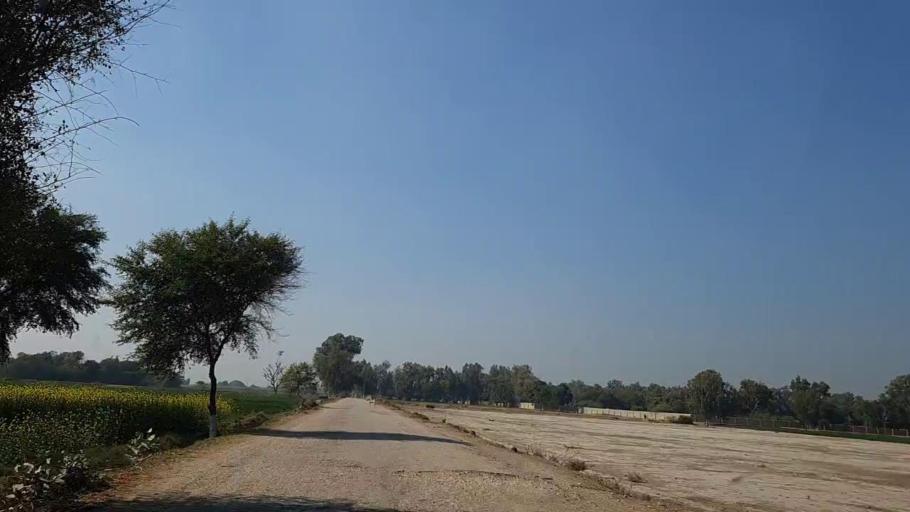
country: PK
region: Sindh
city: Sakrand
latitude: 26.2907
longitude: 68.1072
